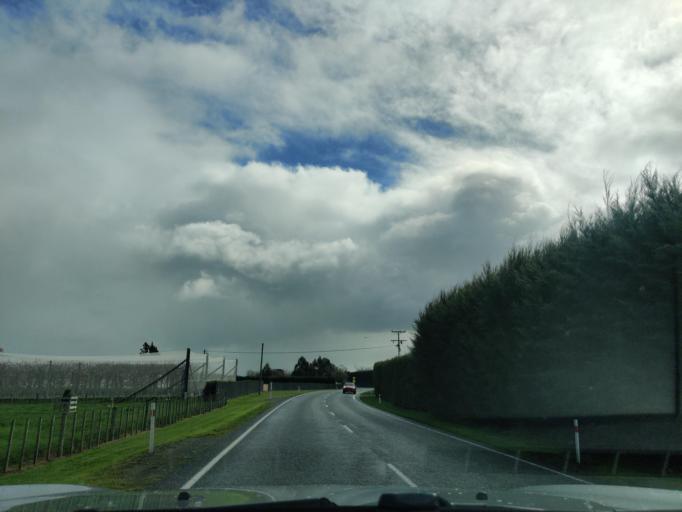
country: NZ
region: Hawke's Bay
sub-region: Hastings District
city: Hastings
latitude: -39.6792
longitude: 176.8384
